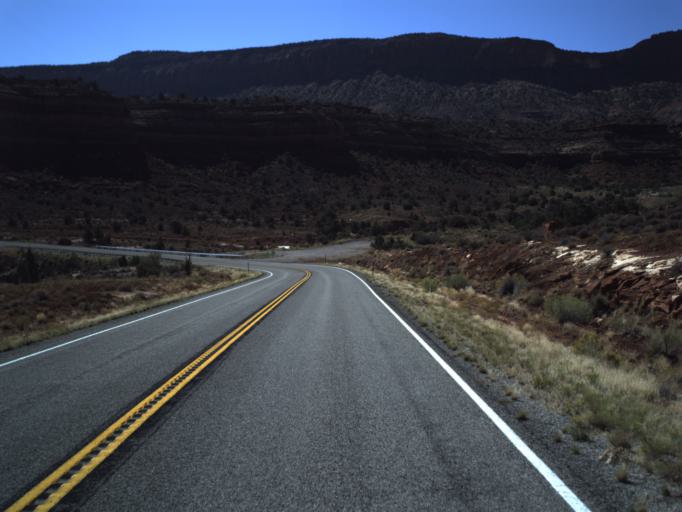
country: US
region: Utah
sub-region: San Juan County
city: Blanding
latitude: 37.7451
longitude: -110.2808
